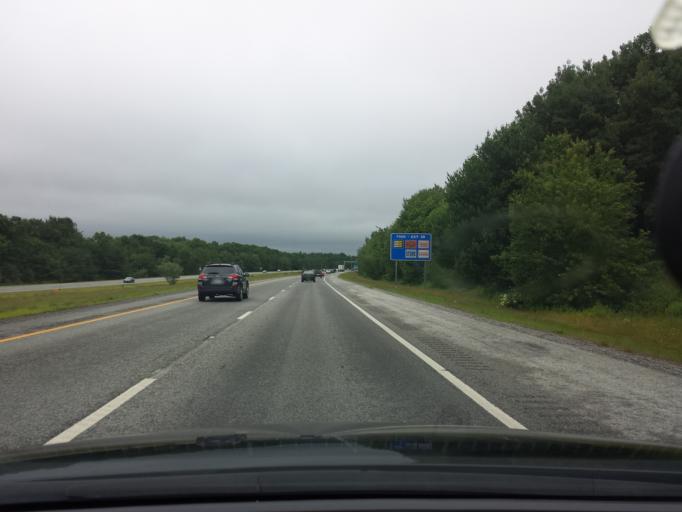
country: US
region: Rhode Island
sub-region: Kent County
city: West Greenwich
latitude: 41.5934
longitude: -71.6593
